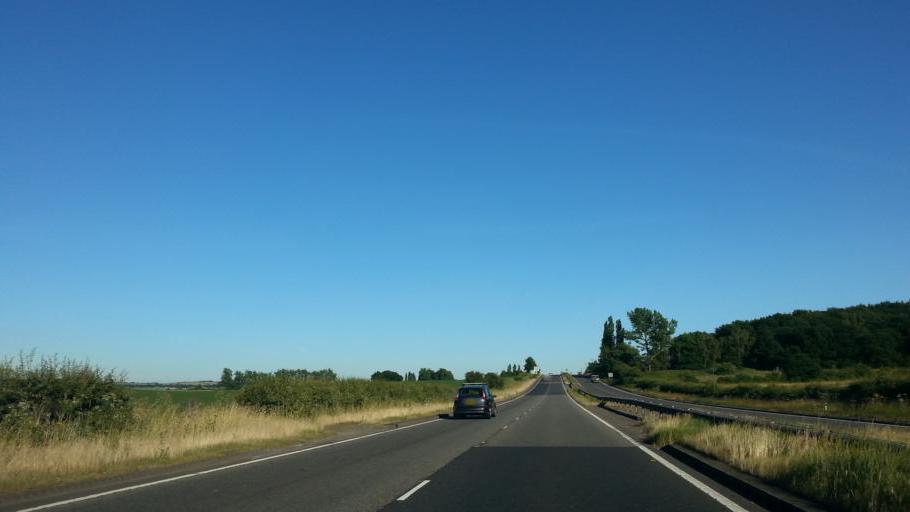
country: GB
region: England
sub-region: Nottinghamshire
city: Babworth
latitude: 53.2836
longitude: -0.9932
